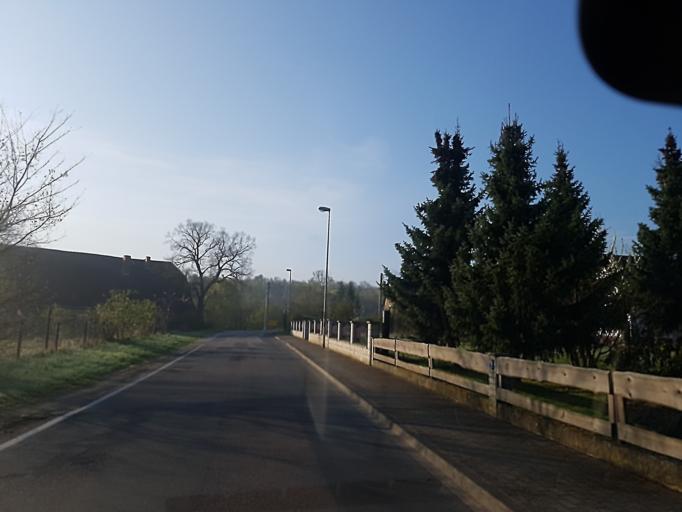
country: DE
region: Saxony
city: Belgern
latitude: 51.4368
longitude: 13.1608
